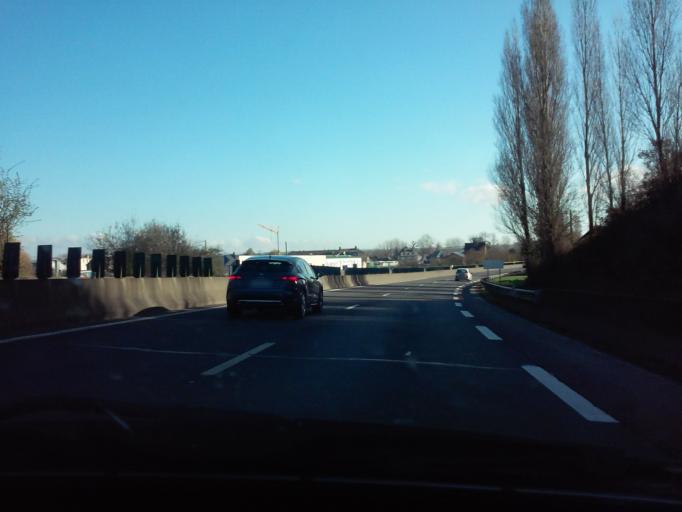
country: FR
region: Lower Normandy
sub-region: Departement de la Manche
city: Avranches
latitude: 48.6876
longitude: -1.3735
